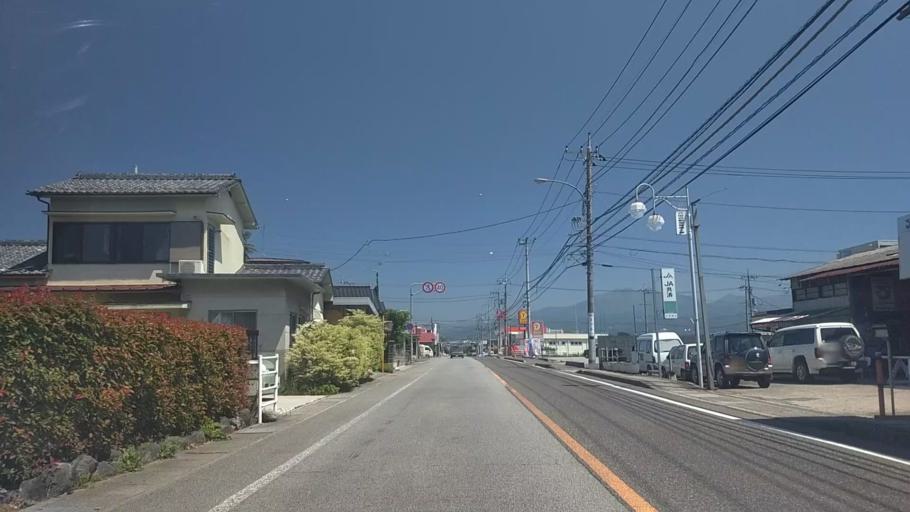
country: JP
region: Yamanashi
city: Nirasaki
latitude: 35.6665
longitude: 138.4646
